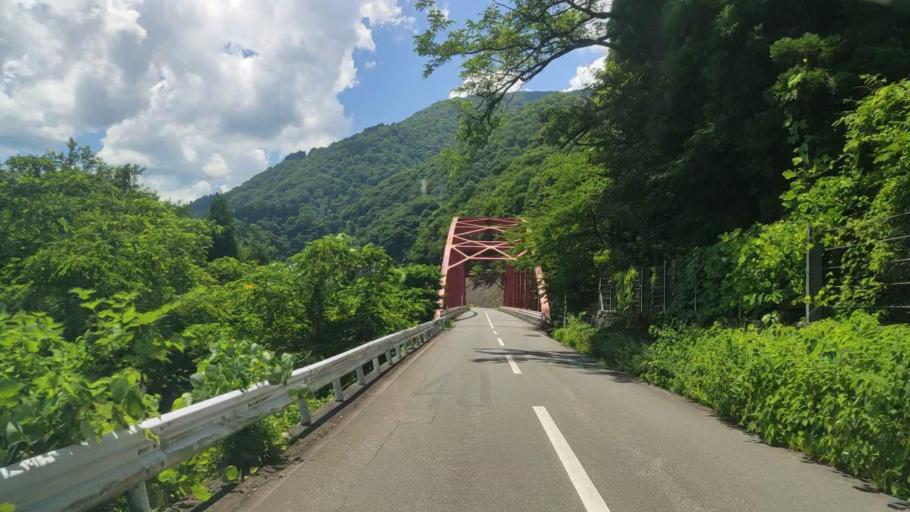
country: JP
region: Fukui
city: Ono
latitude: 35.8998
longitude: 136.5108
